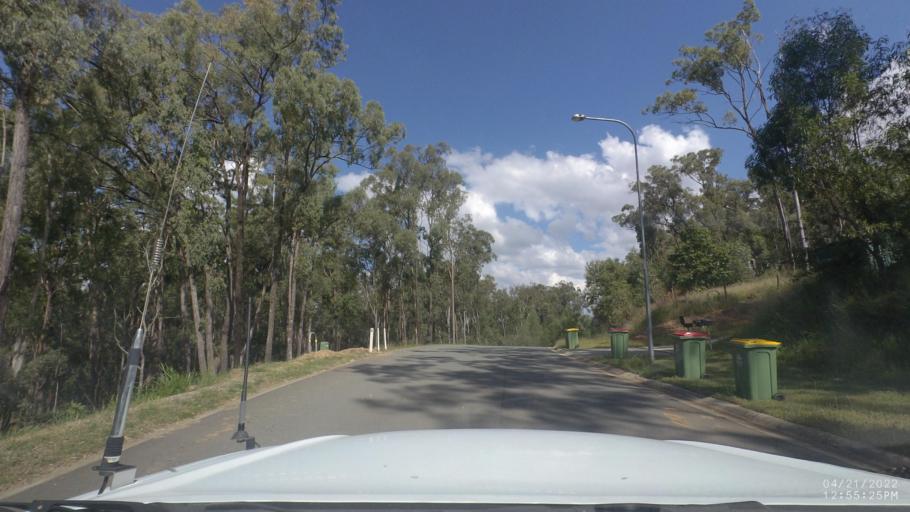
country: AU
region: Queensland
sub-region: Logan
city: Cedar Vale
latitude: -27.8360
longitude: 153.1009
